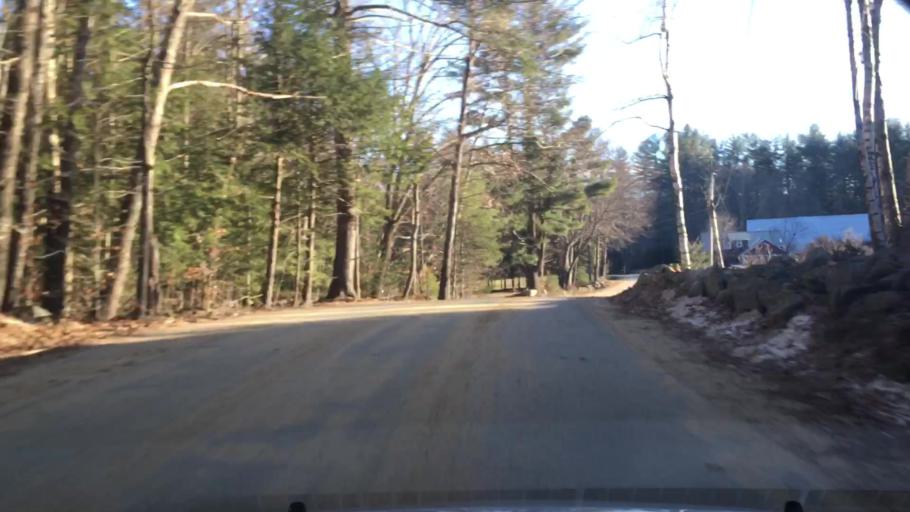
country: US
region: New Hampshire
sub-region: Hillsborough County
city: Mont Vernon
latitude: 42.9084
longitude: -71.6062
